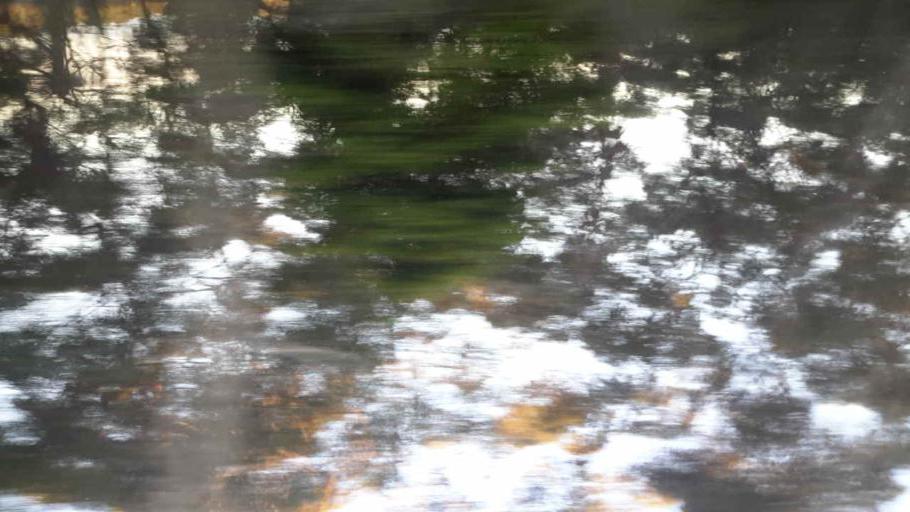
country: AU
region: New South Wales
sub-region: Wollongong
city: Mount Keira
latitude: -34.3872
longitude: 150.8407
